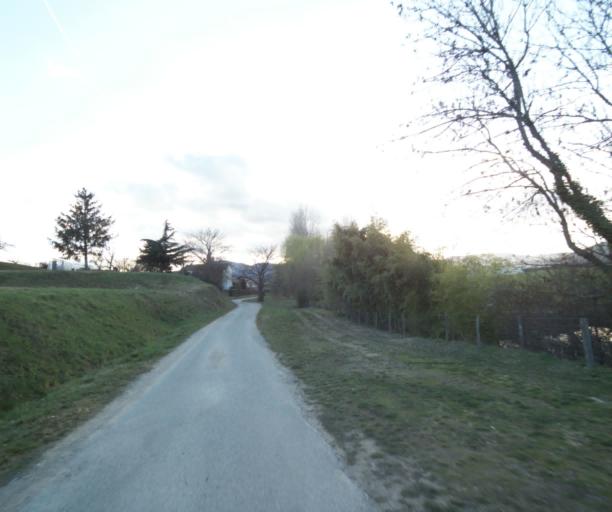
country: FR
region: Rhone-Alpes
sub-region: Departement de l'Ardeche
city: Davezieux
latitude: 45.2438
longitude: 4.6954
